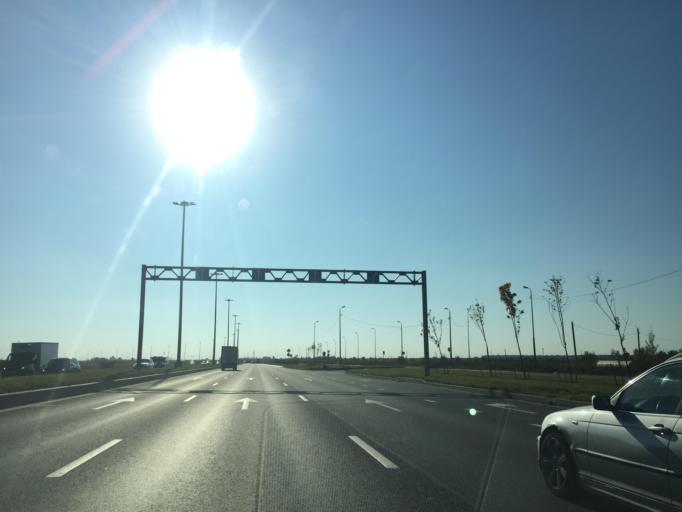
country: RU
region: St.-Petersburg
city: Petro-Slavyanka
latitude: 59.7719
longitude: 30.4997
